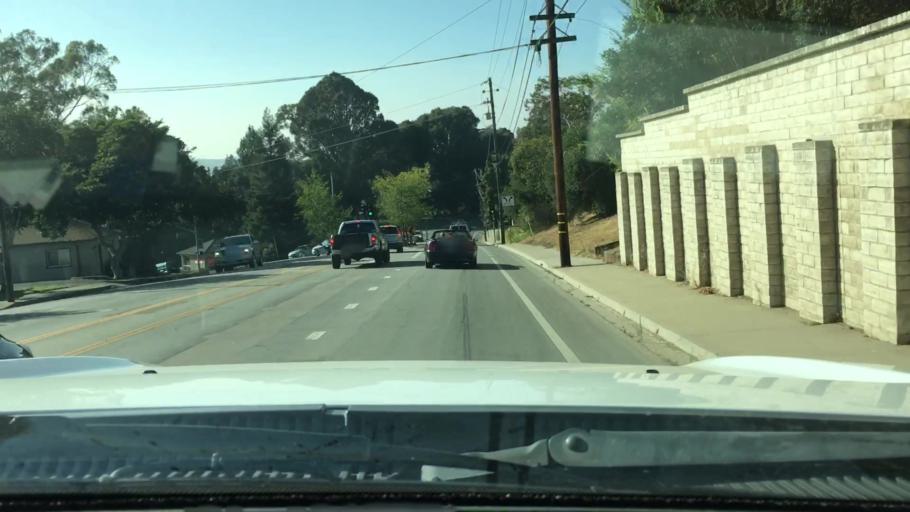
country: US
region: California
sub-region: San Luis Obispo County
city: San Luis Obispo
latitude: 35.2800
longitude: -120.6513
